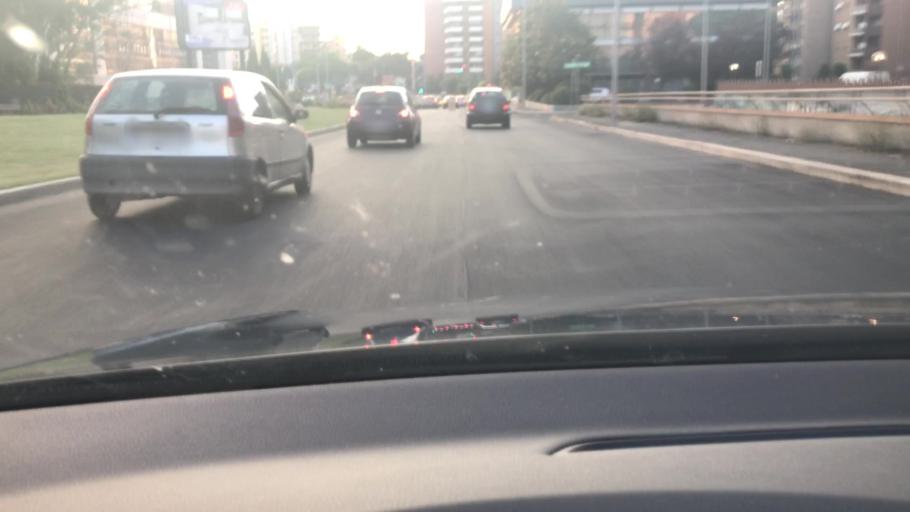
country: IT
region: Latium
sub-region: Citta metropolitana di Roma Capitale
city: Rome
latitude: 41.9298
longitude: 12.5624
